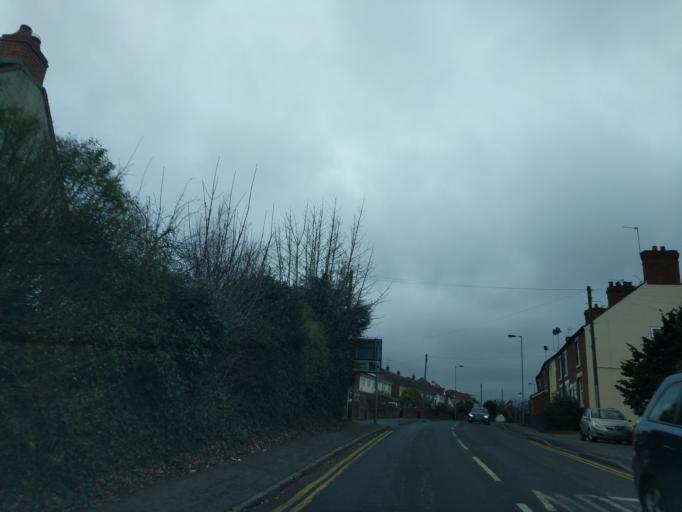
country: GB
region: England
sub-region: Staffordshire
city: Cannock
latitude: 52.6937
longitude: -2.0323
